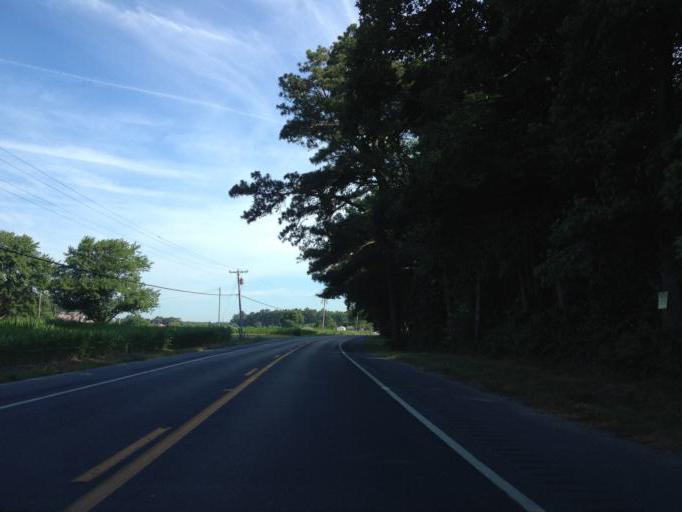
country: US
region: Delaware
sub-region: Sussex County
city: Selbyville
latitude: 38.5084
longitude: -75.1770
